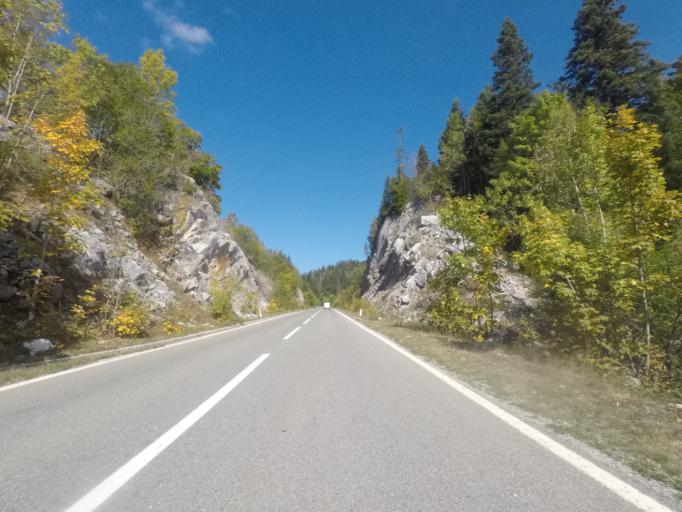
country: ME
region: Opstina Savnik
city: Savnik
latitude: 42.9580
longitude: 18.9121
